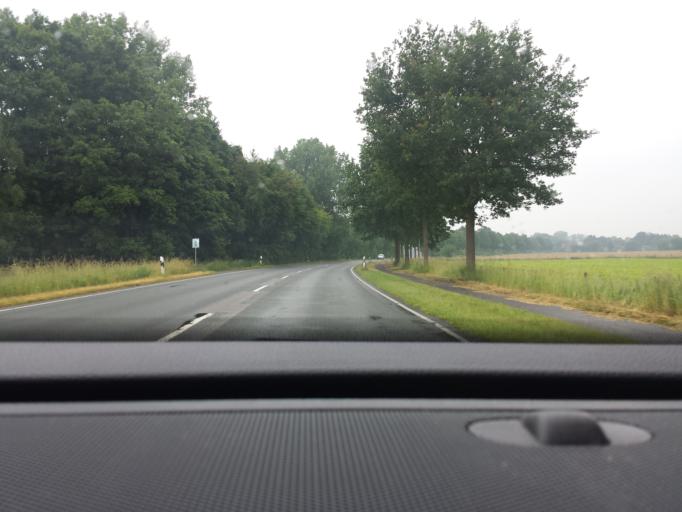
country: DE
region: North Rhine-Westphalia
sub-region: Regierungsbezirk Munster
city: Gronau
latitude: 52.1992
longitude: 6.9735
